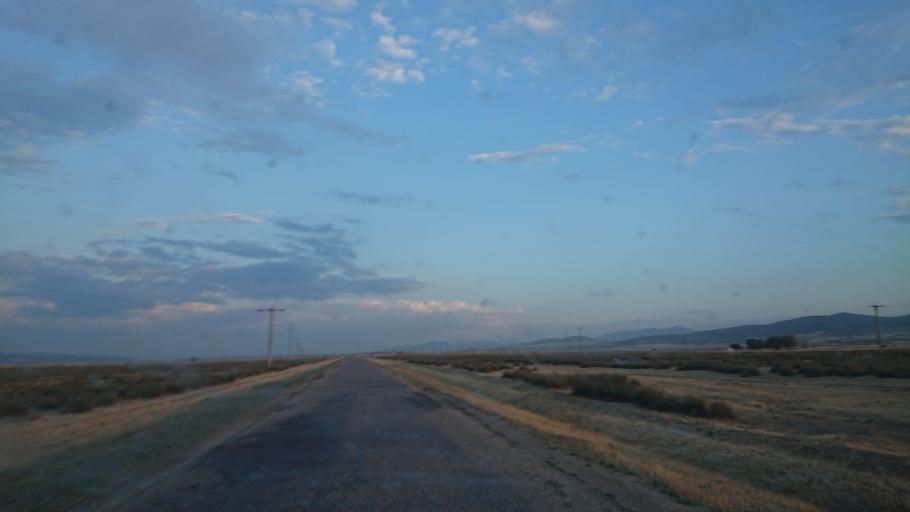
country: TR
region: Aksaray
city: Agacoren
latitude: 38.8815
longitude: 34.0554
